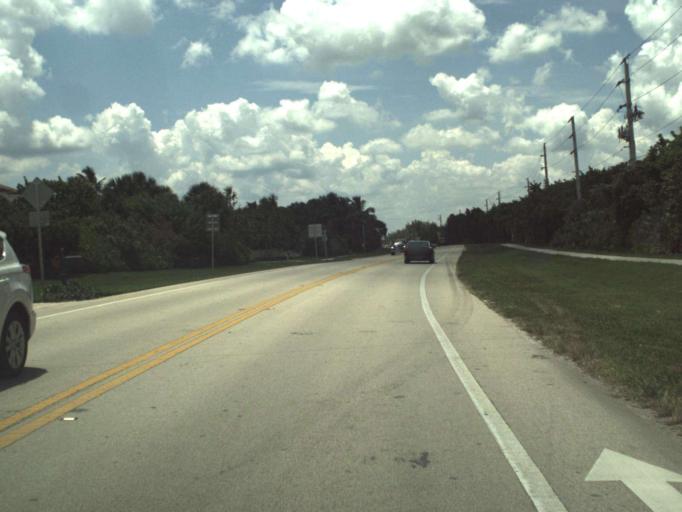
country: US
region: Florida
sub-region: Martin County
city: Jensen Beach
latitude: 27.2627
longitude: -80.2011
